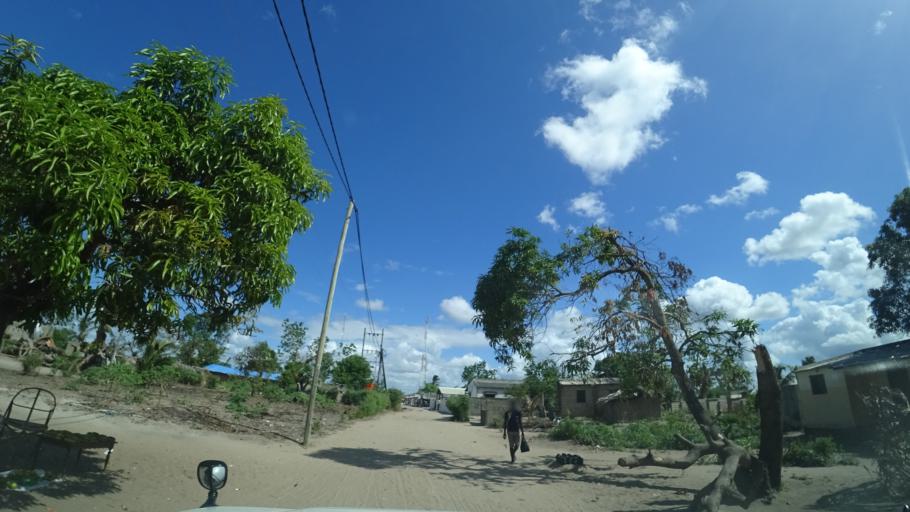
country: MZ
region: Sofala
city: Dondo
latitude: -19.4990
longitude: 34.5976
